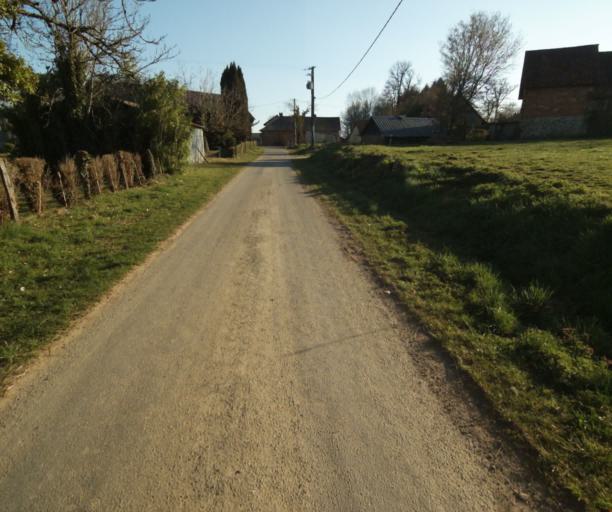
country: FR
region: Limousin
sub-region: Departement de la Correze
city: Saint-Clement
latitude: 45.3388
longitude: 1.6611
